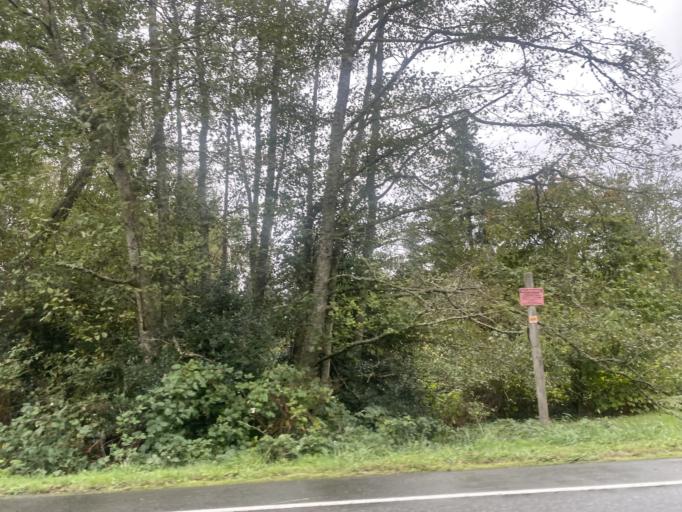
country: US
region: Washington
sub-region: Island County
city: Freeland
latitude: 48.0409
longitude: -122.5068
